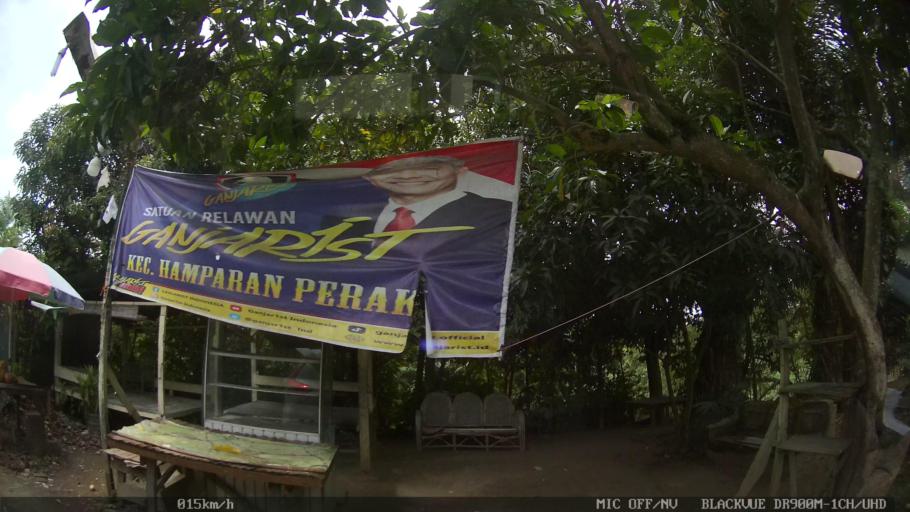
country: ID
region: North Sumatra
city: Sunggal
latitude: 3.6386
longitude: 98.5918
